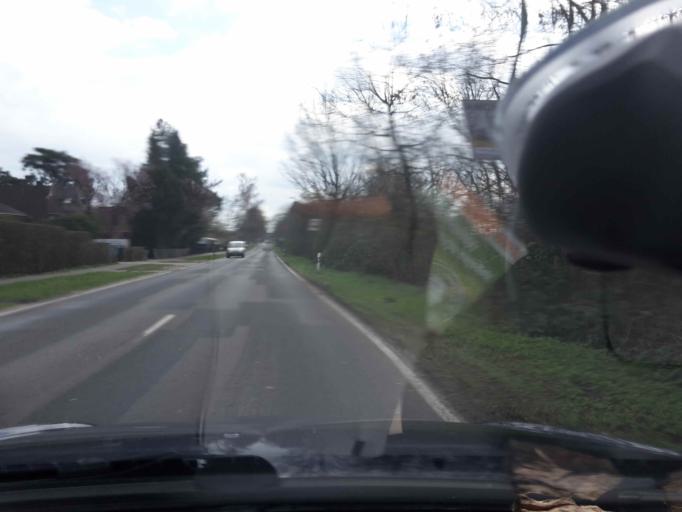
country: DE
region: Lower Saxony
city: Buchholz in der Nordheide
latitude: 53.3228
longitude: 9.8864
